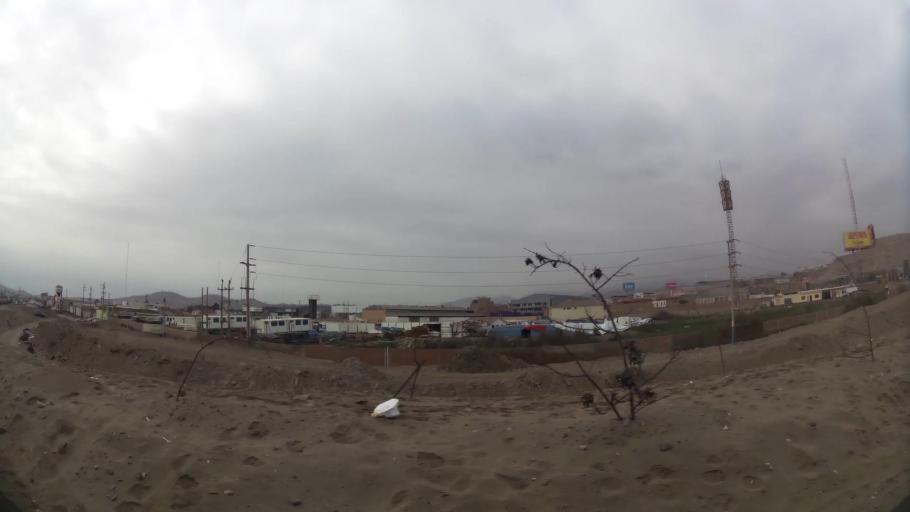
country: PE
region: Lima
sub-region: Lima
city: Surco
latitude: -12.2175
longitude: -76.9791
